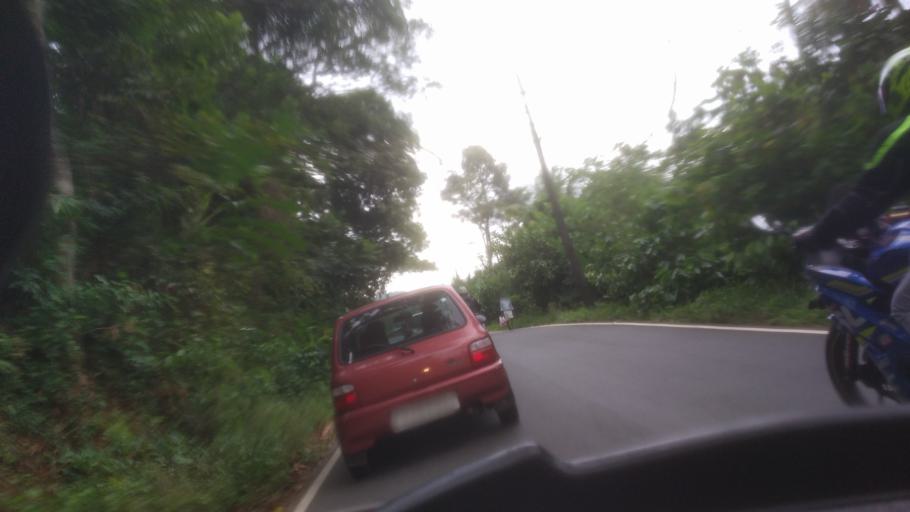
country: IN
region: Kerala
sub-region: Idukki
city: Idukki
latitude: 9.9598
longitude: 77.0082
